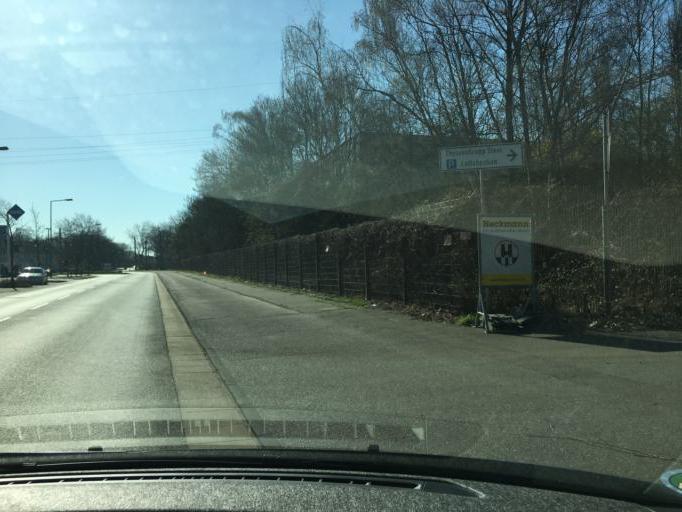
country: DE
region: North Rhine-Westphalia
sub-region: Regierungsbezirk Dusseldorf
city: Dinslaken
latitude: 51.5143
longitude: 6.7405
